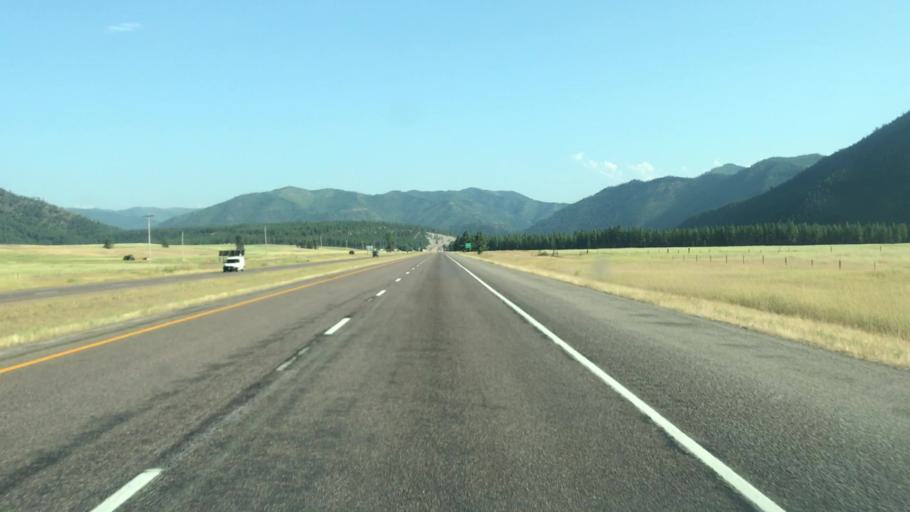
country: US
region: Montana
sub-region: Mineral County
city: Superior
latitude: 47.0457
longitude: -114.7527
